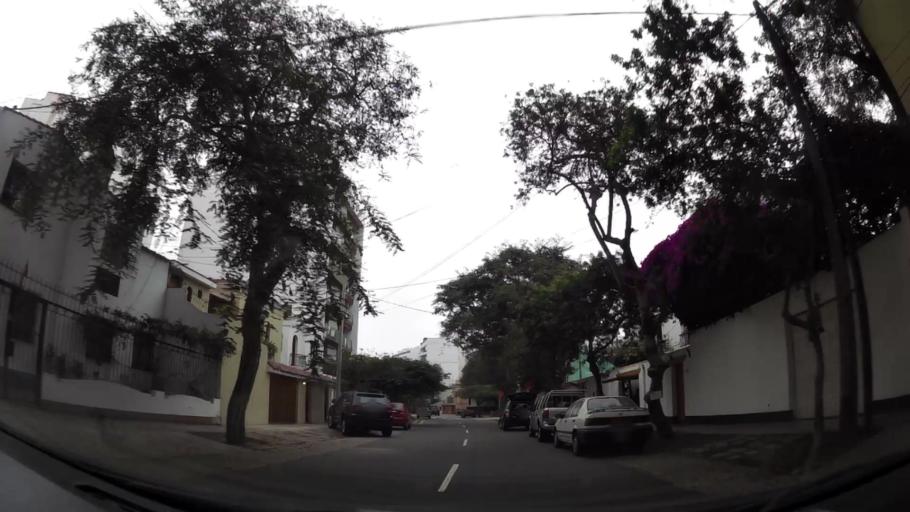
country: PE
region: Lima
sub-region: Lima
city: Surco
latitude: -12.1303
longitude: -77.0268
